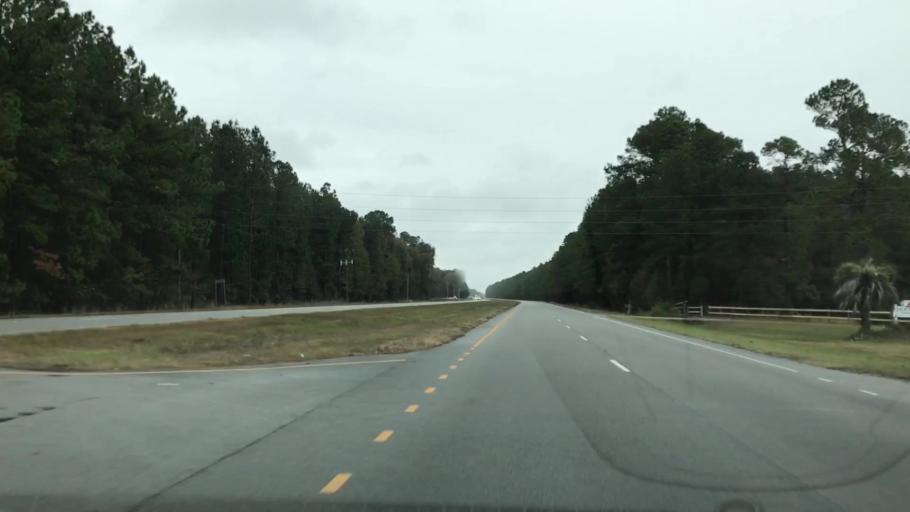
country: US
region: South Carolina
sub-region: Charleston County
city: Awendaw
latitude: 33.1205
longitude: -79.4530
